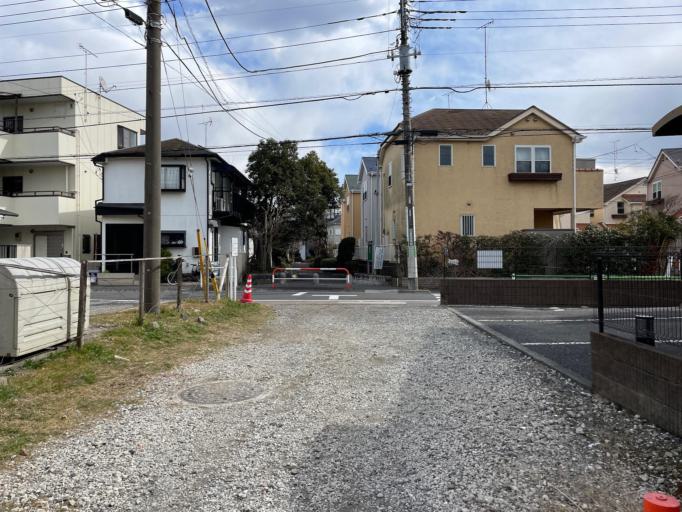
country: JP
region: Tokyo
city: Chofugaoka
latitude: 35.6566
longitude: 139.5205
